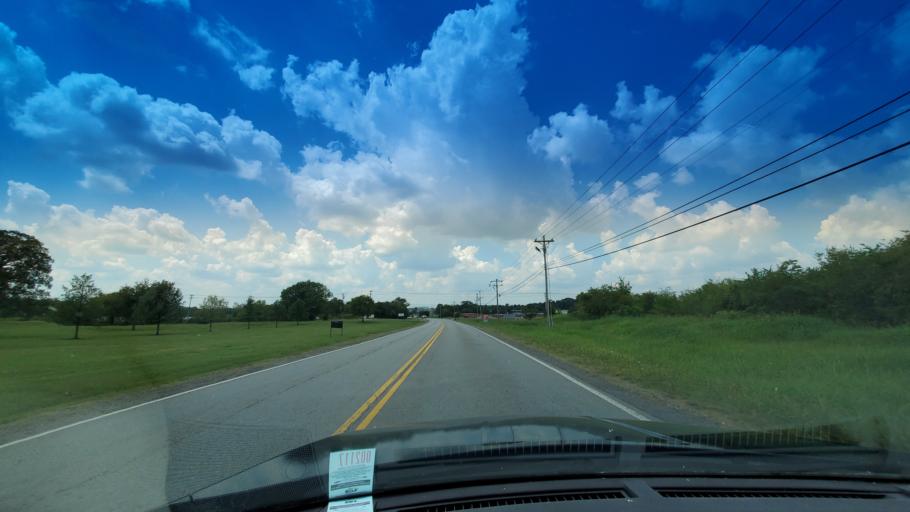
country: US
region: Tennessee
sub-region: Wilson County
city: Lebanon
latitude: 36.1730
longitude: -86.2919
